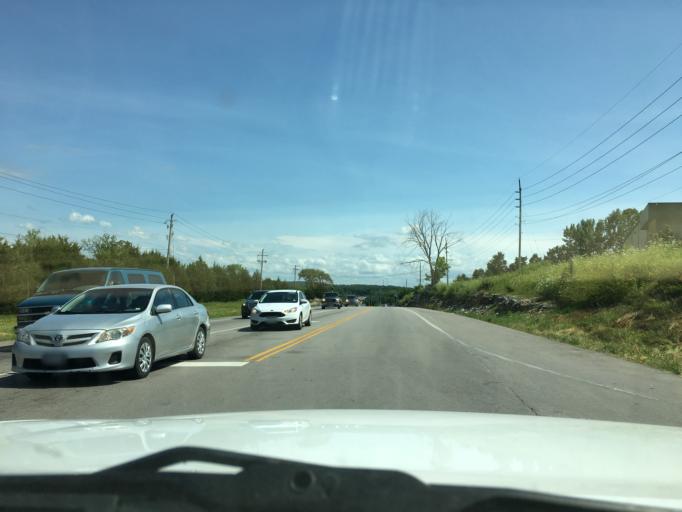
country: US
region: Missouri
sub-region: Franklin County
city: Union
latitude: 38.4601
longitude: -91.0047
